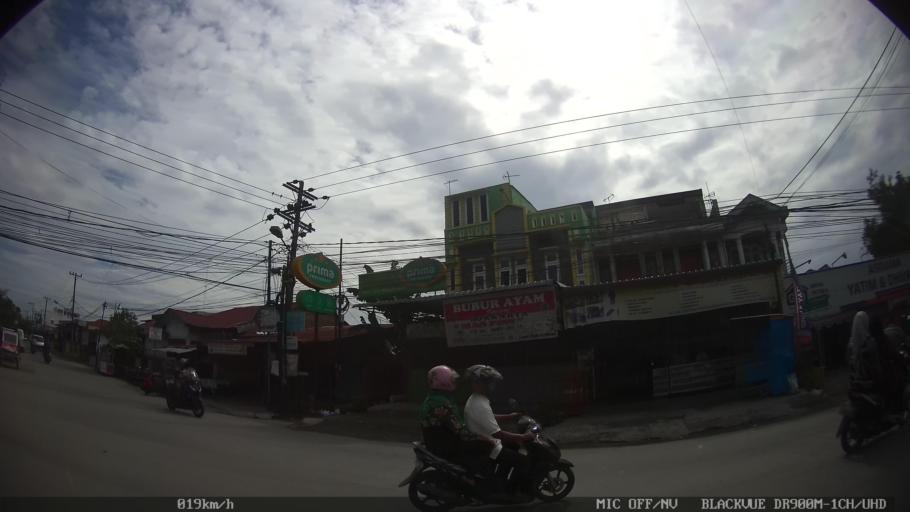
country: ID
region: North Sumatra
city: Sunggal
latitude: 3.6088
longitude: 98.6121
